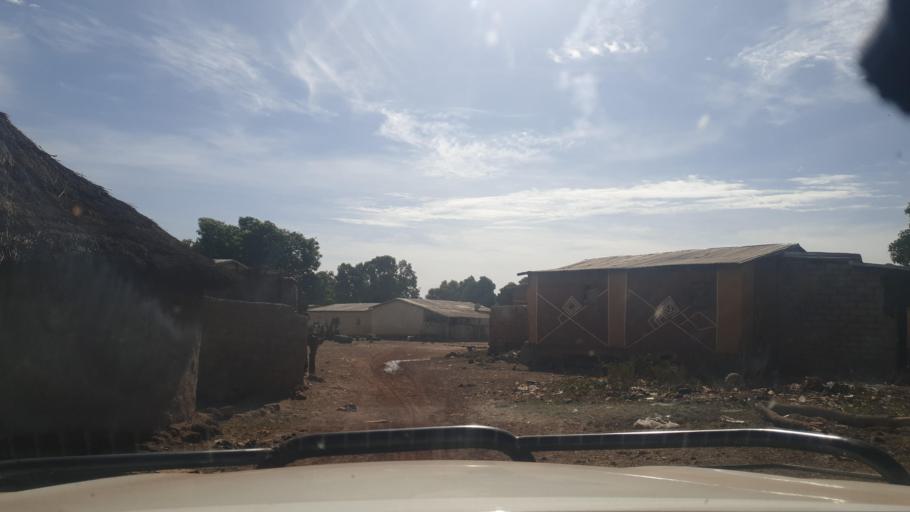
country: GN
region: Kankan
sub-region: Mandiana Prefecture
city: Mandiana
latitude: 10.4907
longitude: -8.0989
